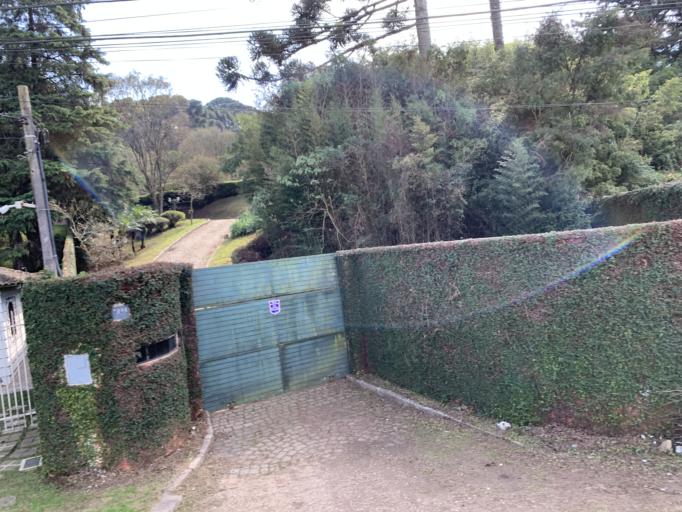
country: BR
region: Parana
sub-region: Curitiba
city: Curitiba
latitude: -25.3872
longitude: -49.3042
